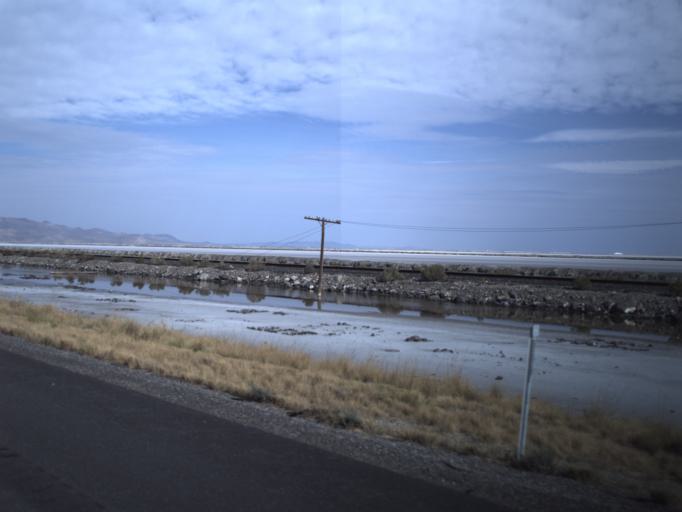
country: US
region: Utah
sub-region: Tooele County
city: Grantsville
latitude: 40.7213
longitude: -112.5572
